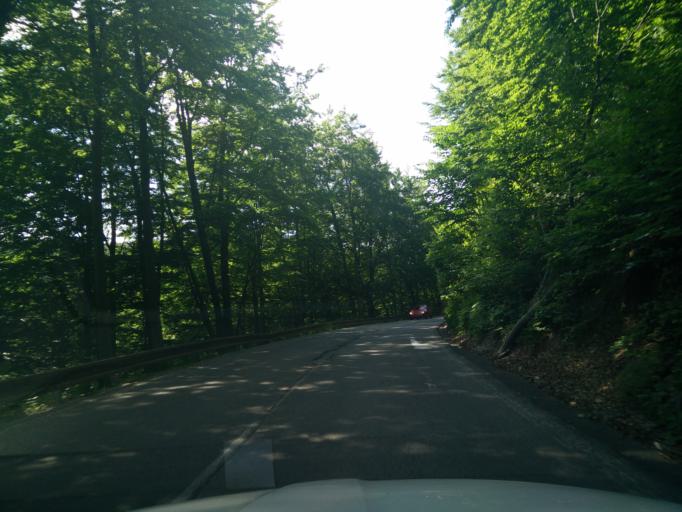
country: SK
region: Zilinsky
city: Rajec
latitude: 48.9506
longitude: 18.6238
